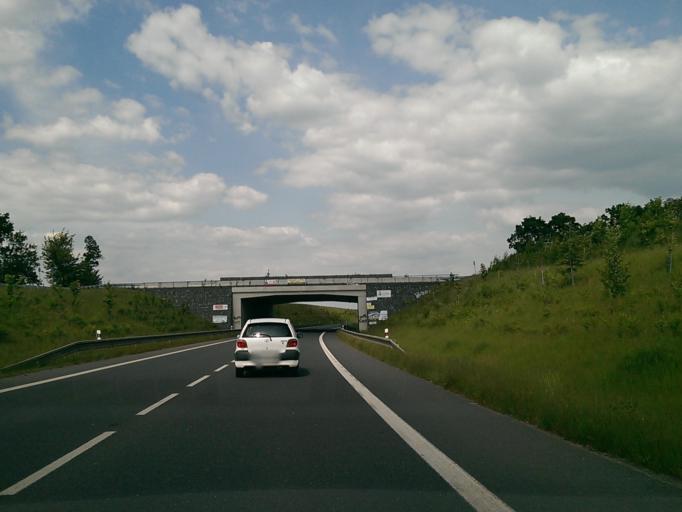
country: CZ
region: Central Bohemia
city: Libeznice
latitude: 50.1952
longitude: 14.4866
